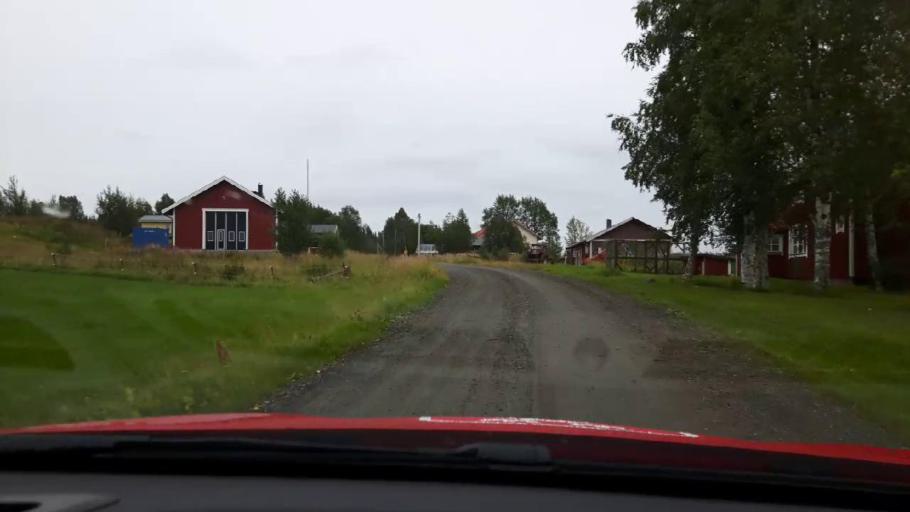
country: SE
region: Jaemtland
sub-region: Are Kommun
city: Are
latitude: 63.5151
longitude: 12.7111
